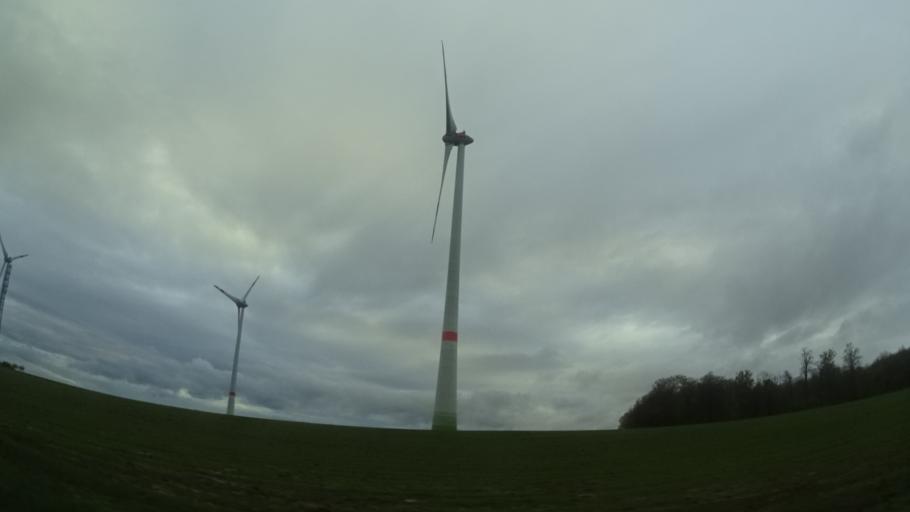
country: DE
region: Hesse
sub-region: Regierungsbezirk Giessen
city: Freiensteinau
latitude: 50.4443
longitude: 9.3944
